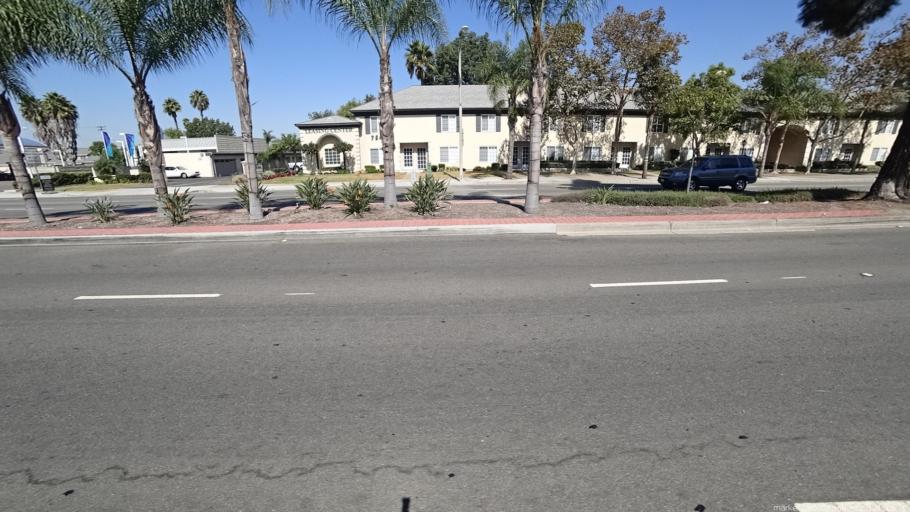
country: US
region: California
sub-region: Orange County
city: Stanton
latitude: 33.8028
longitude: -118.0010
